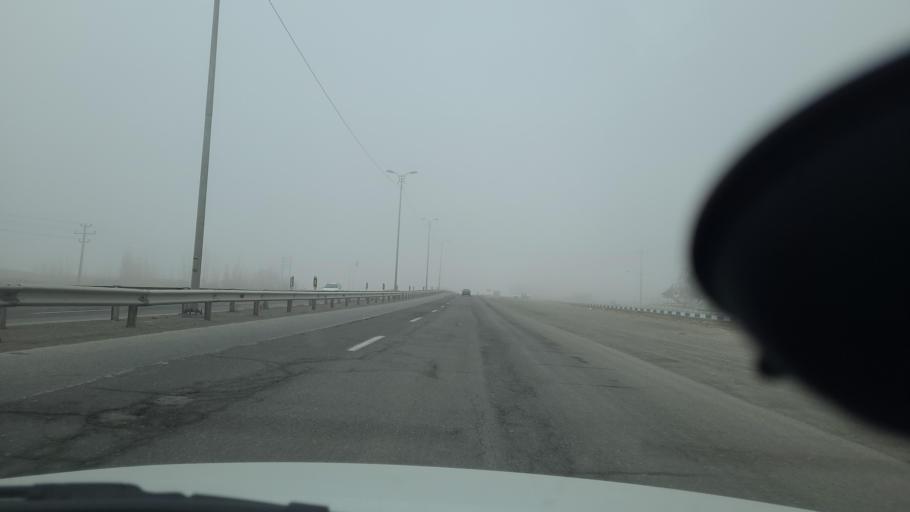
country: IR
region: Razavi Khorasan
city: Fariman
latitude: 35.7699
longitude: 59.7423
